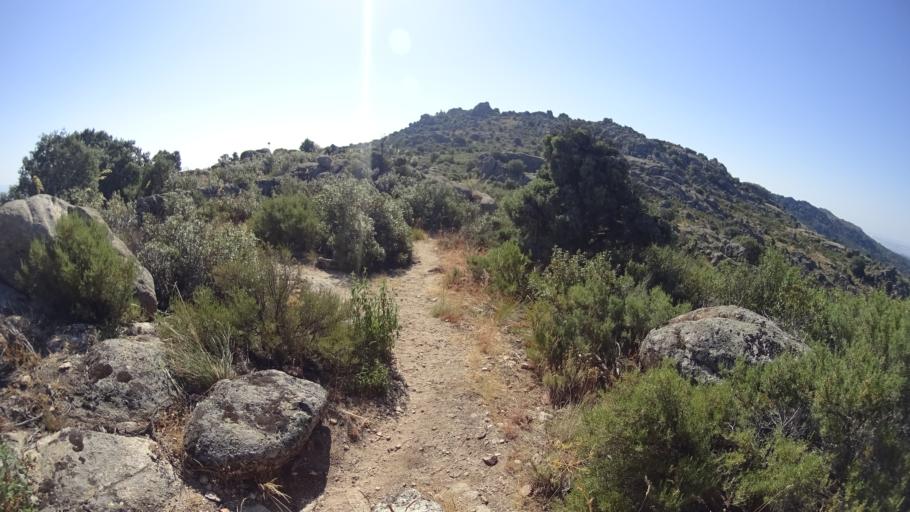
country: ES
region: Madrid
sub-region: Provincia de Madrid
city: Hoyo de Manzanares
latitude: 40.6466
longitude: -3.9343
